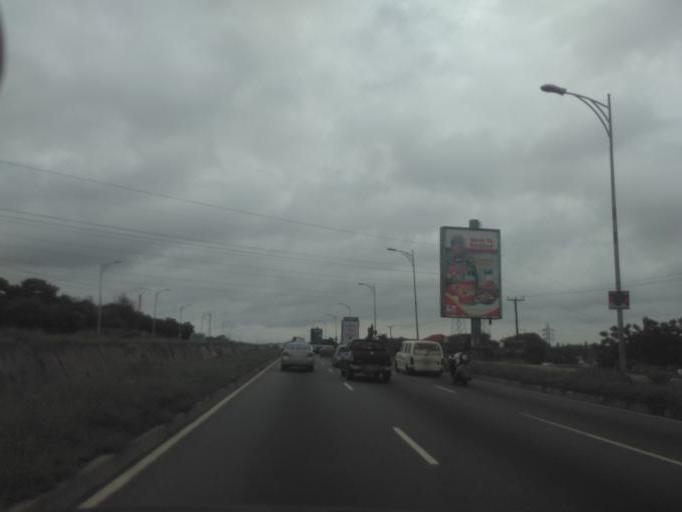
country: GH
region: Greater Accra
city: Medina Estates
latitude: 5.6345
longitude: -0.1771
